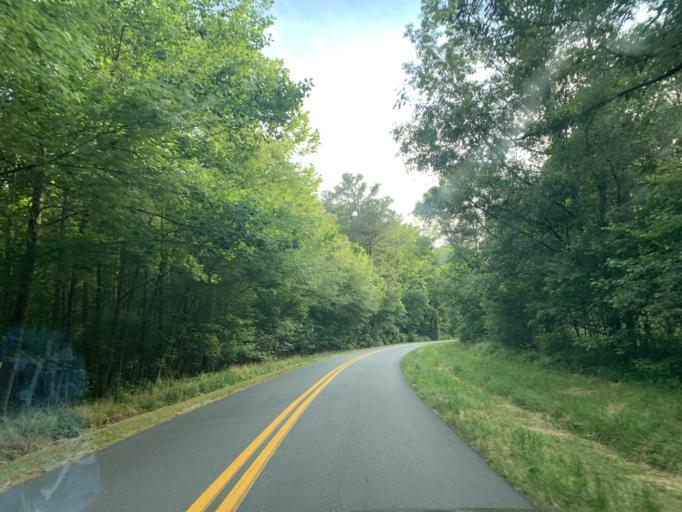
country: US
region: Maryland
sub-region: Worcester County
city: Snow Hill
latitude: 38.0943
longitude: -75.4601
